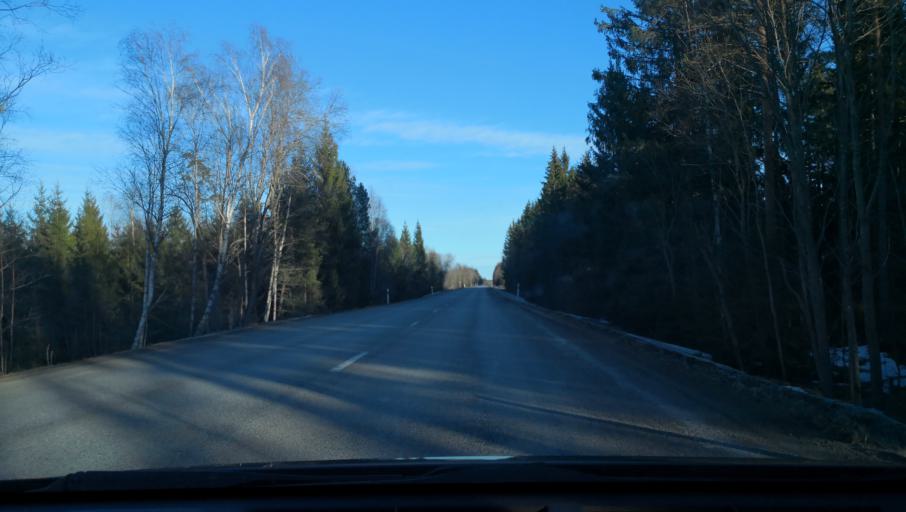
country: SE
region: Uppsala
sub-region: Osthammars Kommun
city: Gimo
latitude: 60.1650
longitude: 18.1354
